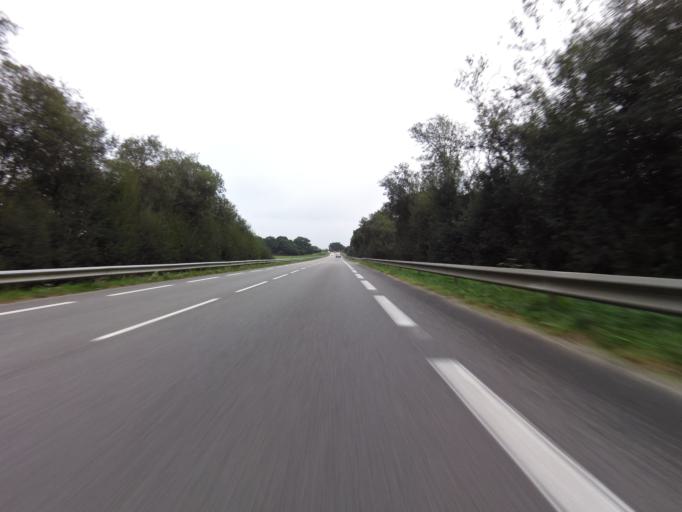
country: FR
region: Brittany
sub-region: Departement du Morbihan
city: Plescop
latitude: 47.6996
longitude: -2.7851
